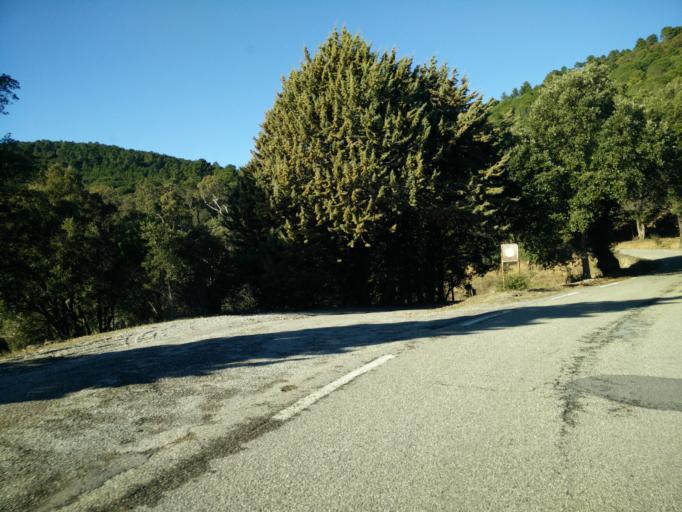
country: FR
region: Provence-Alpes-Cote d'Azur
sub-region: Departement du Var
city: La Garde-Freinet
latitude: 43.2566
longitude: 6.4123
